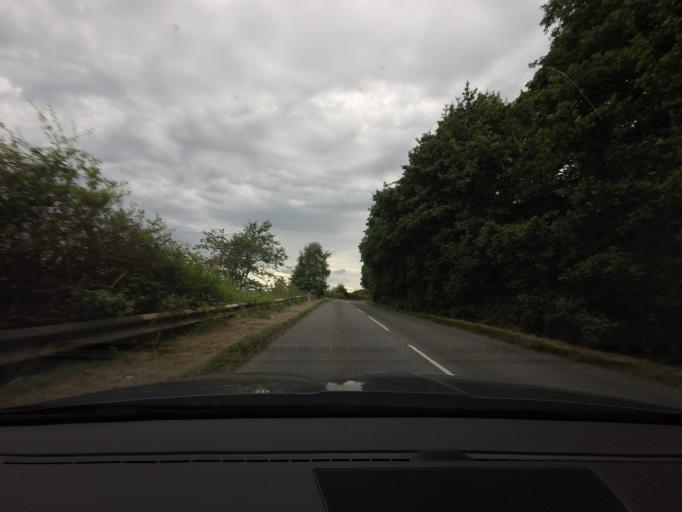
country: GB
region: Scotland
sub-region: Highland
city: Evanton
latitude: 57.6278
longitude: -4.3734
